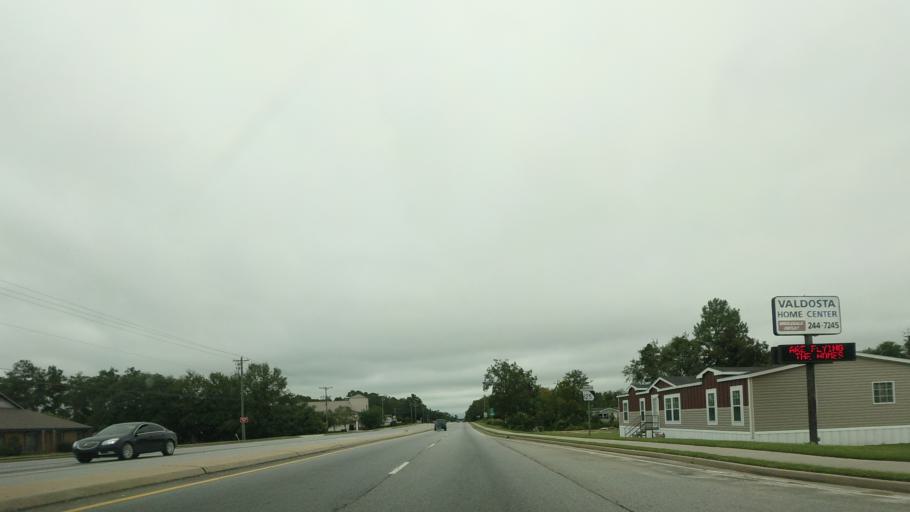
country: US
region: Georgia
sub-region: Lowndes County
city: Valdosta
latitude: 30.8901
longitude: -83.2706
